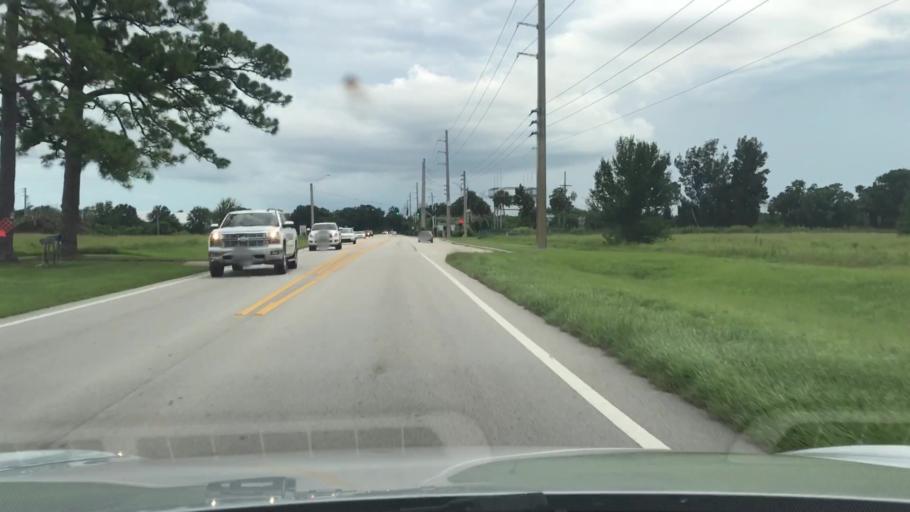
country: US
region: Florida
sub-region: Indian River County
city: Winter Beach
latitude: 27.7429
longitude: -80.4620
